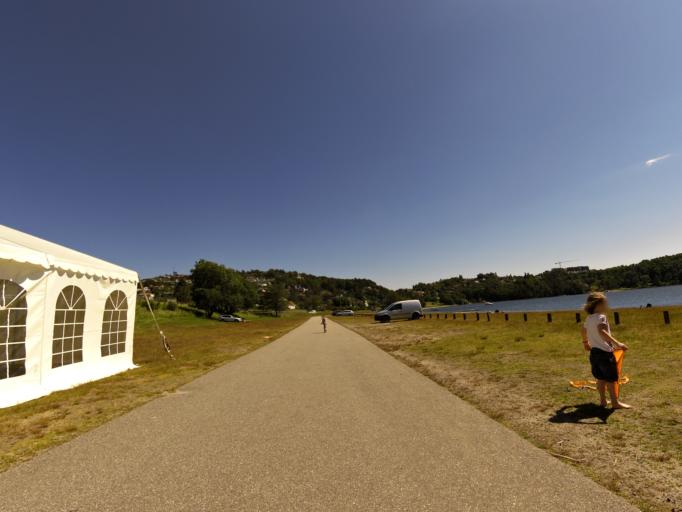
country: NO
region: Vest-Agder
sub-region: Kristiansand
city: Justvik
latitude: 58.1910
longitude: 8.0821
